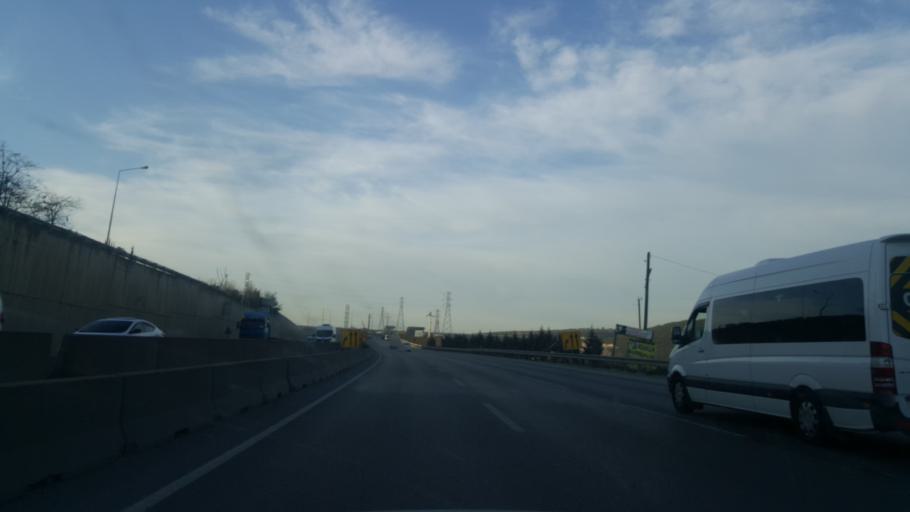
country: TR
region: Kocaeli
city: Tavsanli
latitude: 40.8045
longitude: 29.5274
